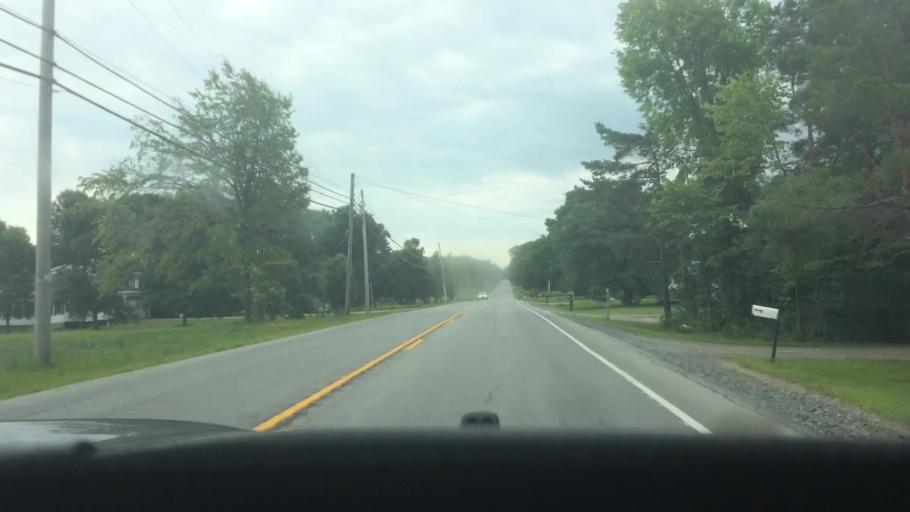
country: US
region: New York
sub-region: St. Lawrence County
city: Ogdensburg
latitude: 44.6564
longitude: -75.4488
